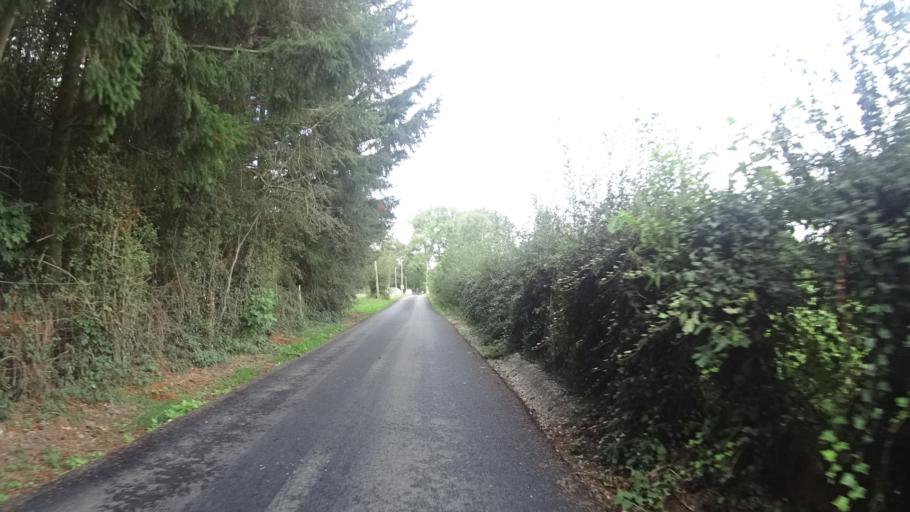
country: FR
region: Picardie
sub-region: Departement de l'Aisne
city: Wassigny
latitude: 50.0459
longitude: 3.6468
